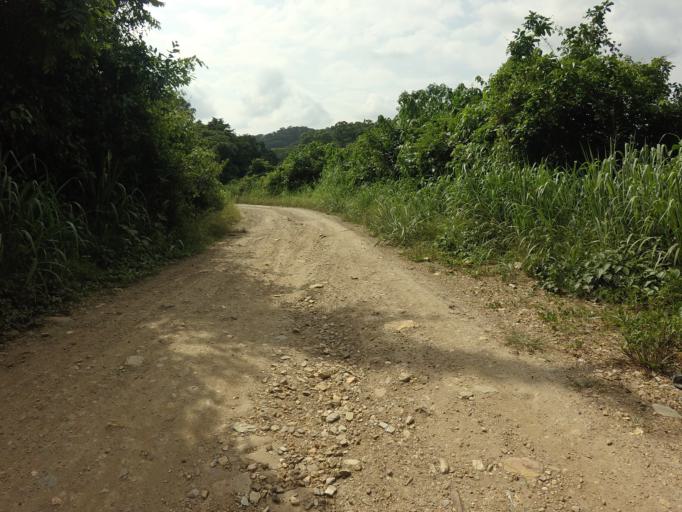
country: GH
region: Volta
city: Kpandu
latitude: 6.8752
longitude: 0.4364
